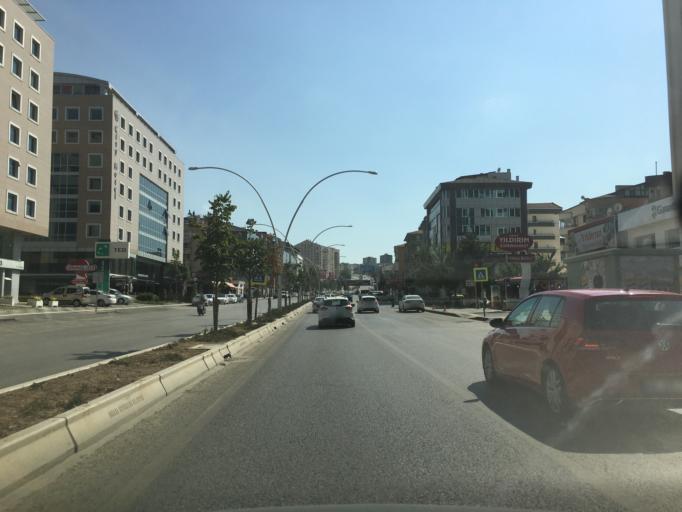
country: TR
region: Ankara
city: Cankaya
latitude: 39.8760
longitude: 32.8636
